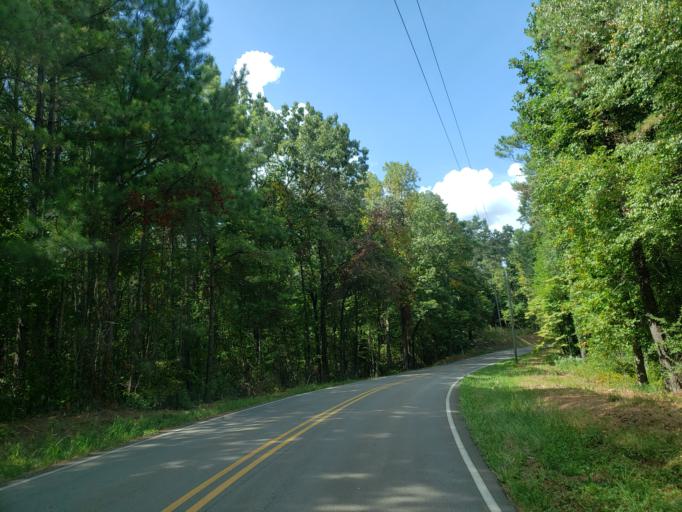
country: US
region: Georgia
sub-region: Pickens County
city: Jasper
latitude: 34.4265
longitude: -84.4405
